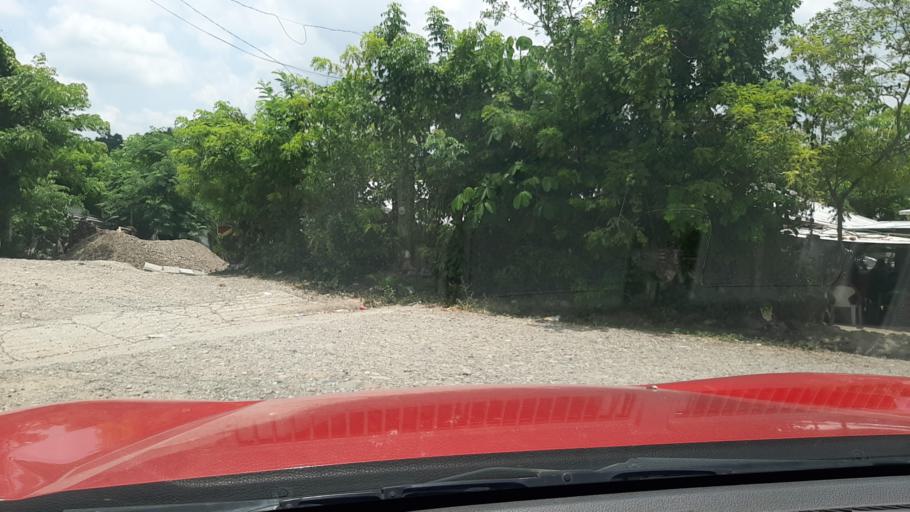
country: MX
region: Veracruz
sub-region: Papantla
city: Polutla
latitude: 20.4494
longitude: -97.2437
